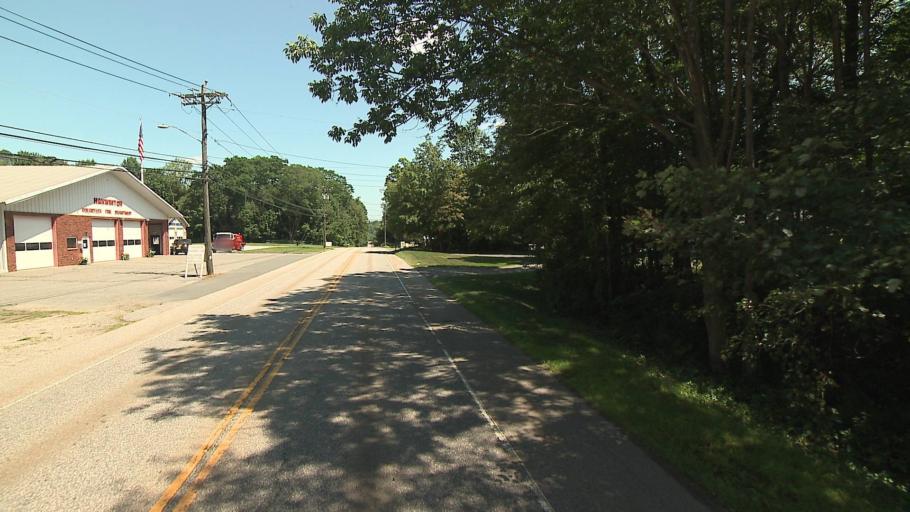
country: US
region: Connecticut
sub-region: Litchfield County
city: Northwest Harwinton
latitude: 41.7734
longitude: -73.0466
